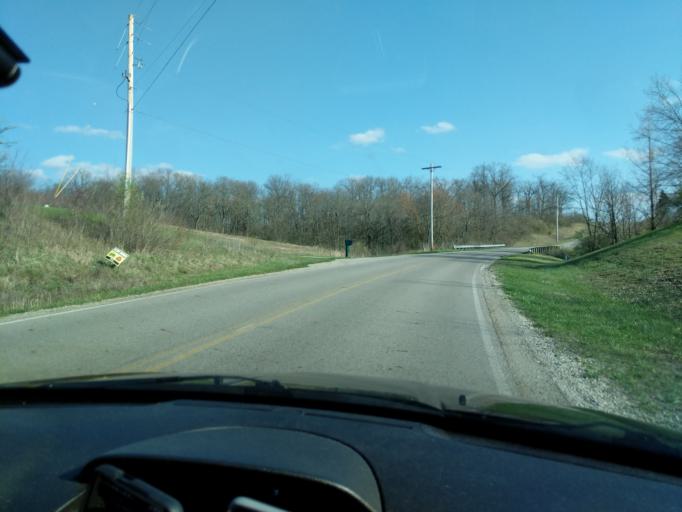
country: US
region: Ohio
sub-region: Champaign County
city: Urbana
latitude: 40.1008
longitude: -83.6651
